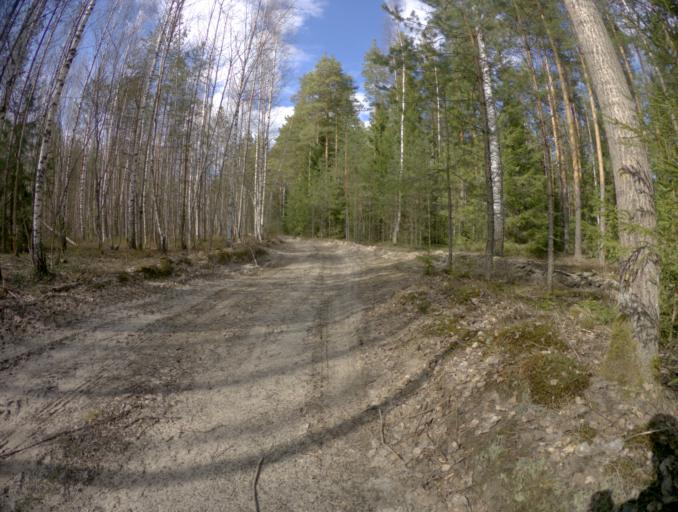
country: RU
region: Vladimir
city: Vorsha
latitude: 55.8796
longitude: 40.1776
